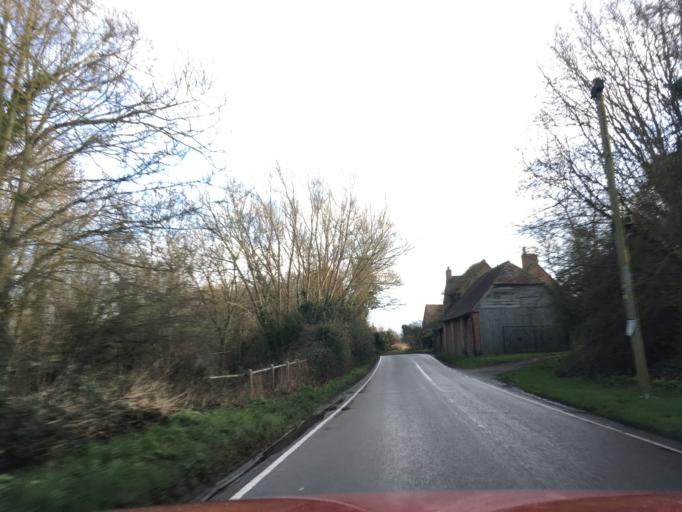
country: GB
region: England
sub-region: Warwickshire
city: Alcester
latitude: 52.2267
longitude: -1.8240
